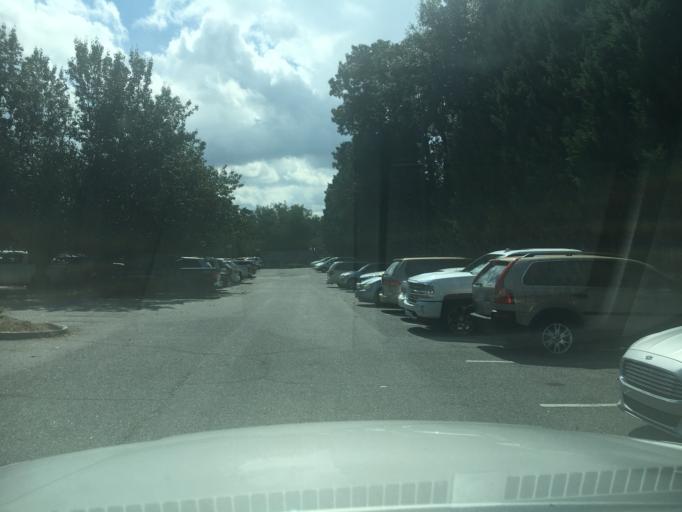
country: US
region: North Carolina
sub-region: Catawba County
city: Hickory
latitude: 35.7380
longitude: -81.3387
